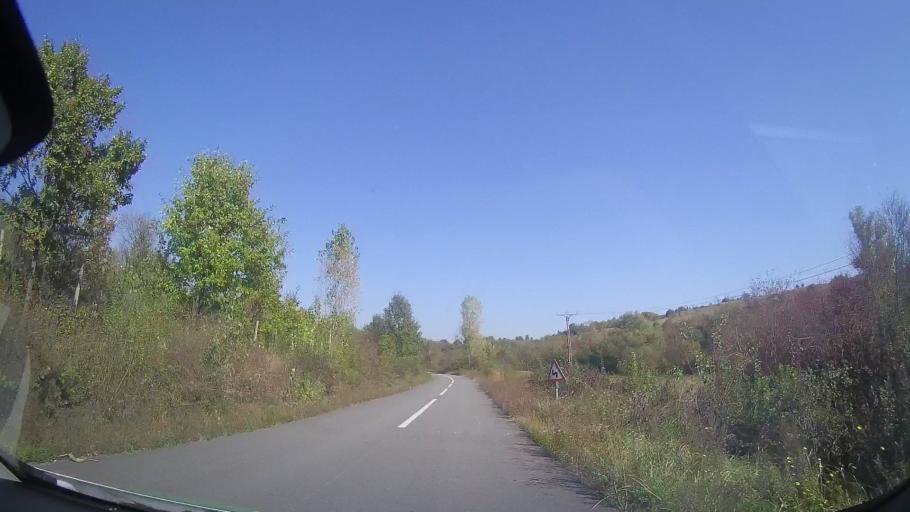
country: RO
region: Timis
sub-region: Comuna Bara
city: Bara
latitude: 45.8741
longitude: 21.8845
